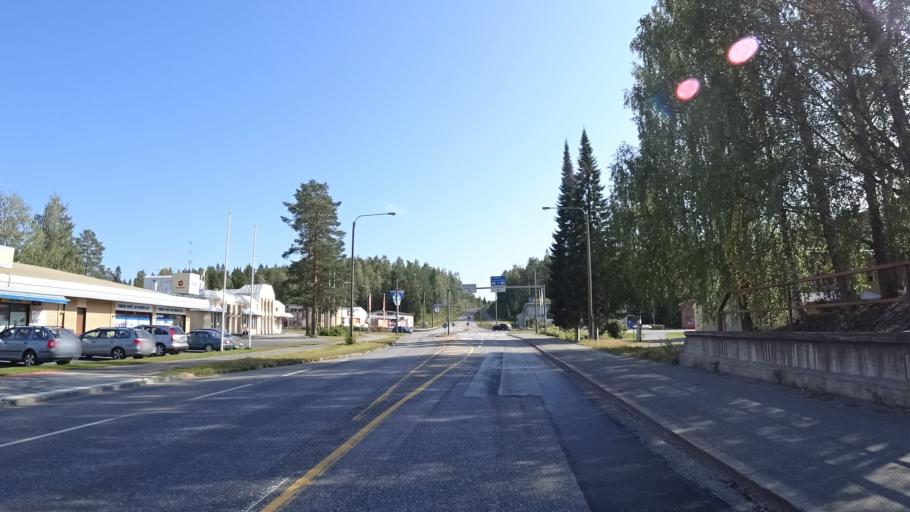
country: FI
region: North Karelia
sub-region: Joensuu
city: Eno
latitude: 62.8000
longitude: 30.1550
